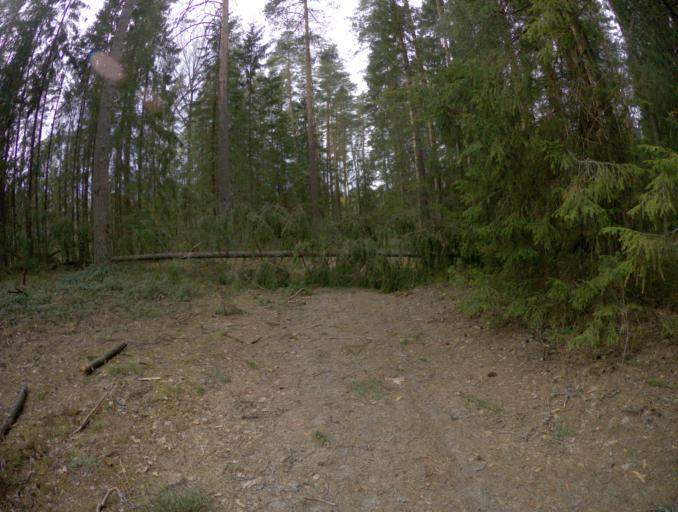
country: RU
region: Vladimir
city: Raduzhnyy
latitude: 55.9362
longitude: 40.2591
